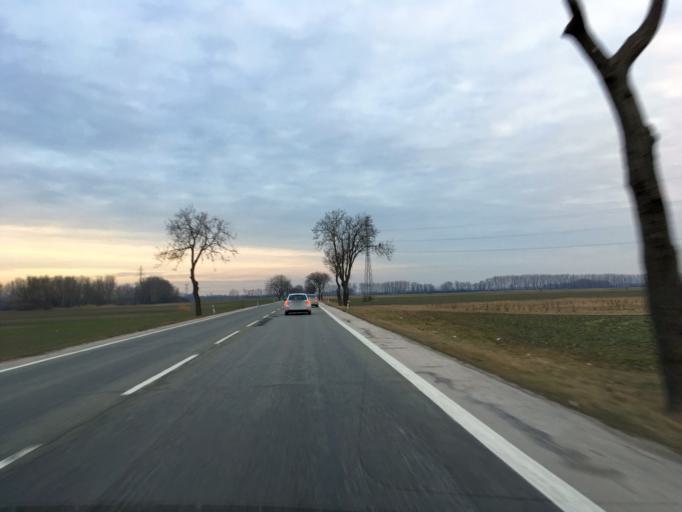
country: SK
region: Trnavsky
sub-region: Okres Dunajska Streda
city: Velky Meder
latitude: 47.8977
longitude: 17.7416
